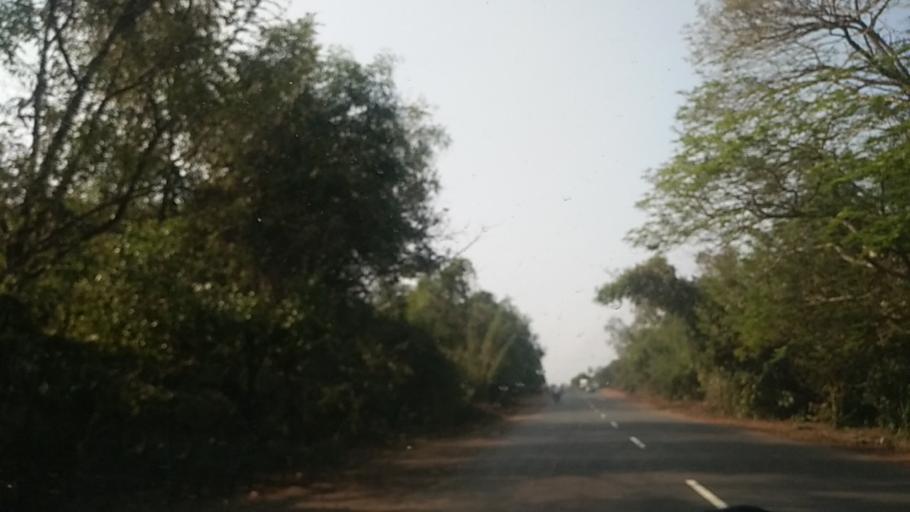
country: IN
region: Goa
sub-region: North Goa
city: Pernem
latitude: 15.7089
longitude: 73.8144
